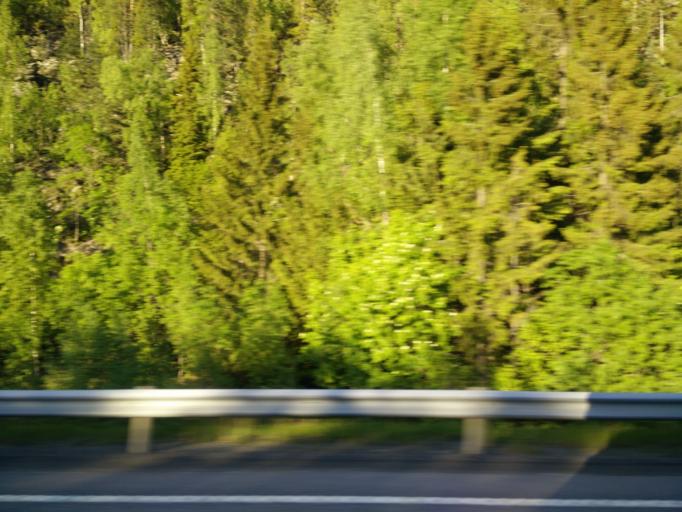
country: NO
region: Buskerud
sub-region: Hole
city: Vik
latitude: 60.0184
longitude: 10.2684
